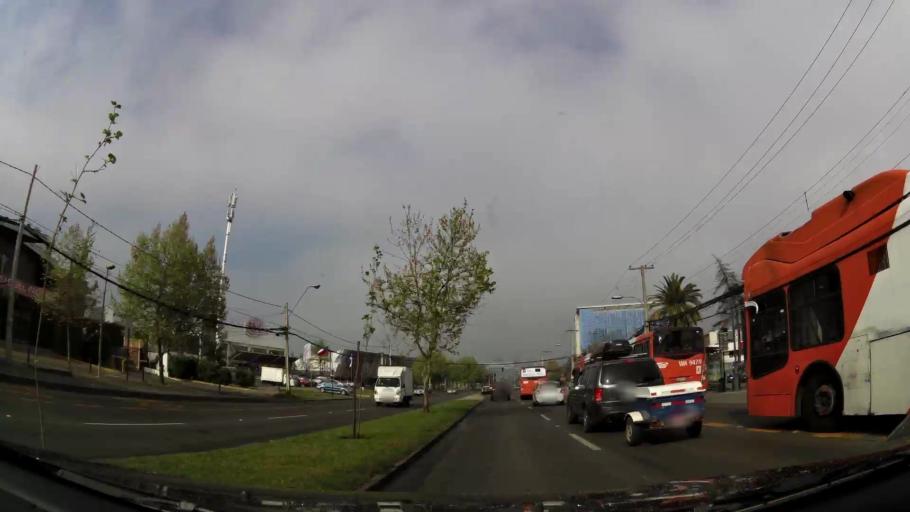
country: CL
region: Santiago Metropolitan
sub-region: Provincia de Santiago
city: Villa Presidente Frei, Nunoa, Santiago, Chile
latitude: -33.3783
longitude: -70.5285
